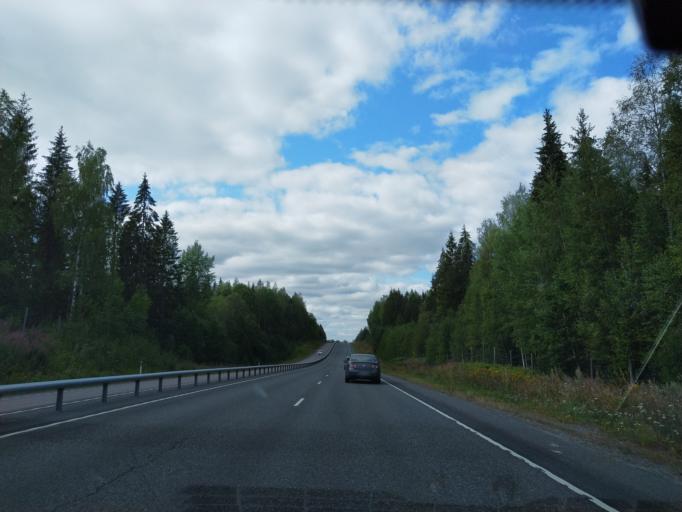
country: FI
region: Haeme
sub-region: Riihimaeki
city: Loppi
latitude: 60.7345
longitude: 24.5508
